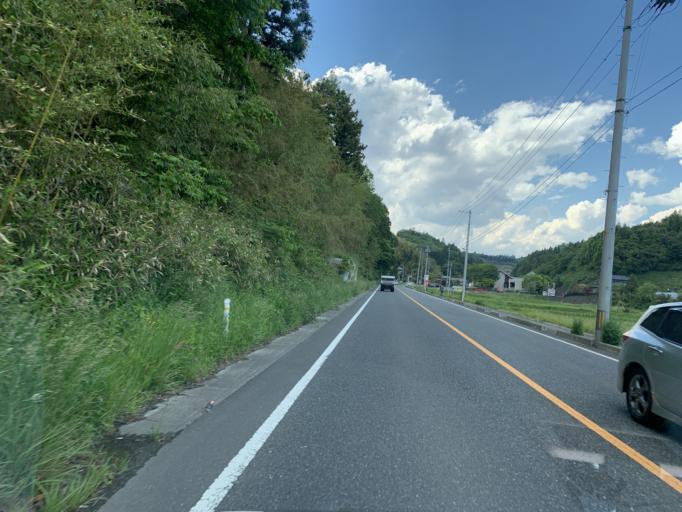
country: JP
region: Miyagi
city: Wakuya
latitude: 38.5551
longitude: 141.1376
